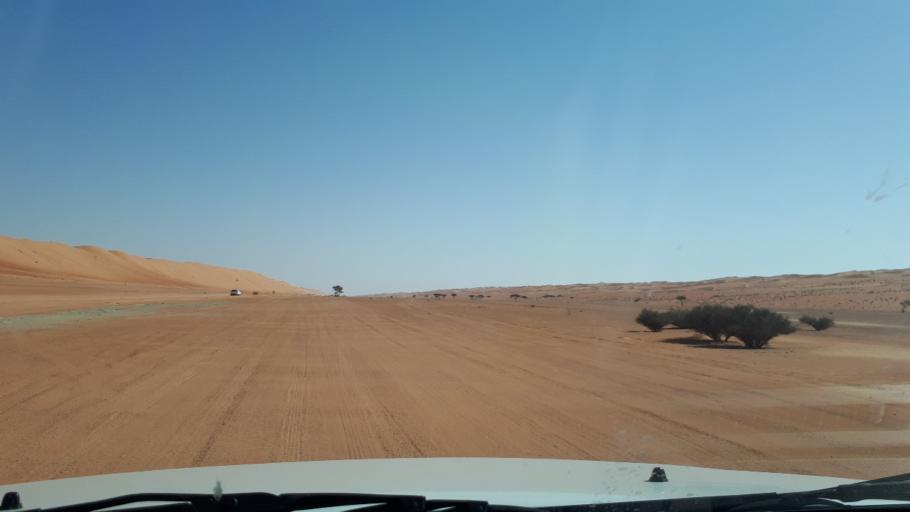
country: OM
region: Ash Sharqiyah
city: Badiyah
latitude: 22.4347
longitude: 58.7320
